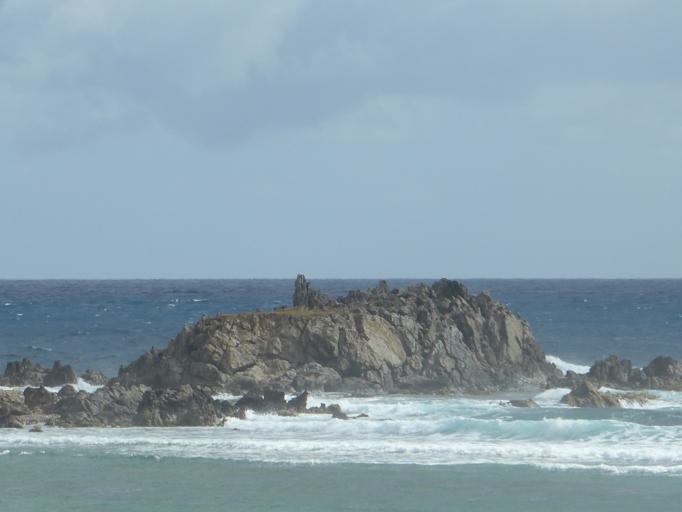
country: SX
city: Philipsburg
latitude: 18.0667
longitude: -63.0126
